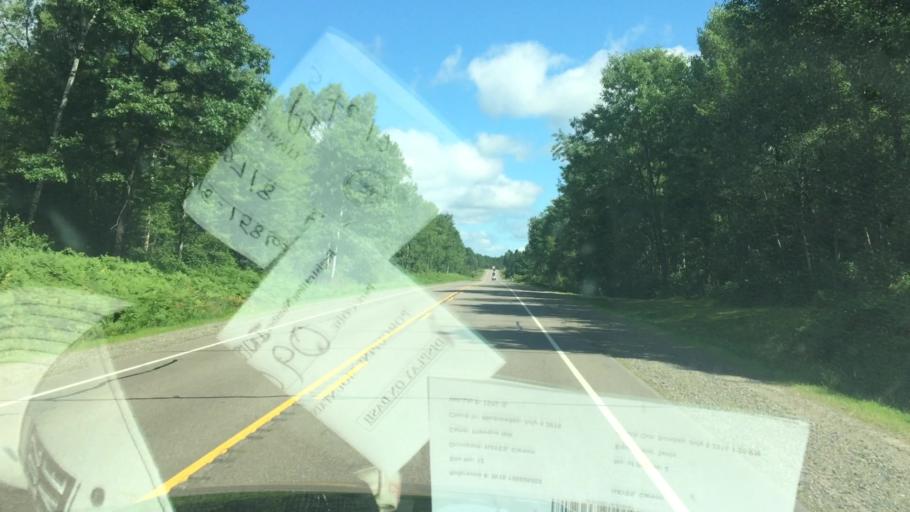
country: US
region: Wisconsin
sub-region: Oneida County
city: Rhinelander
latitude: 45.5803
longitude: -89.5693
